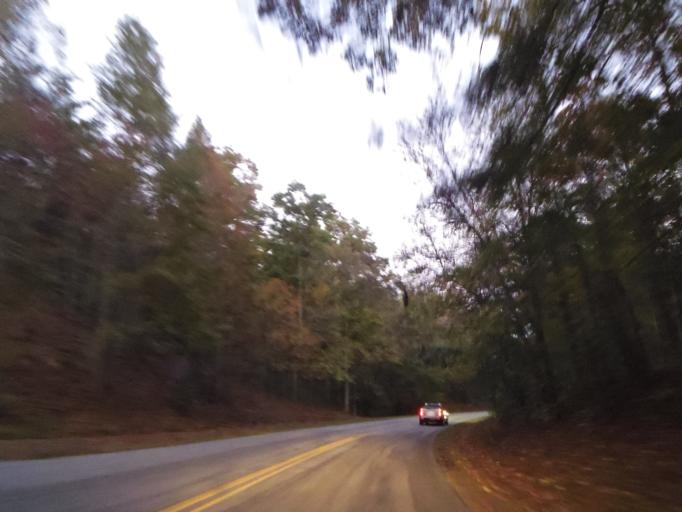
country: US
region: Tennessee
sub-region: Blount County
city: Wildwood
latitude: 35.7184
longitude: -83.8316
